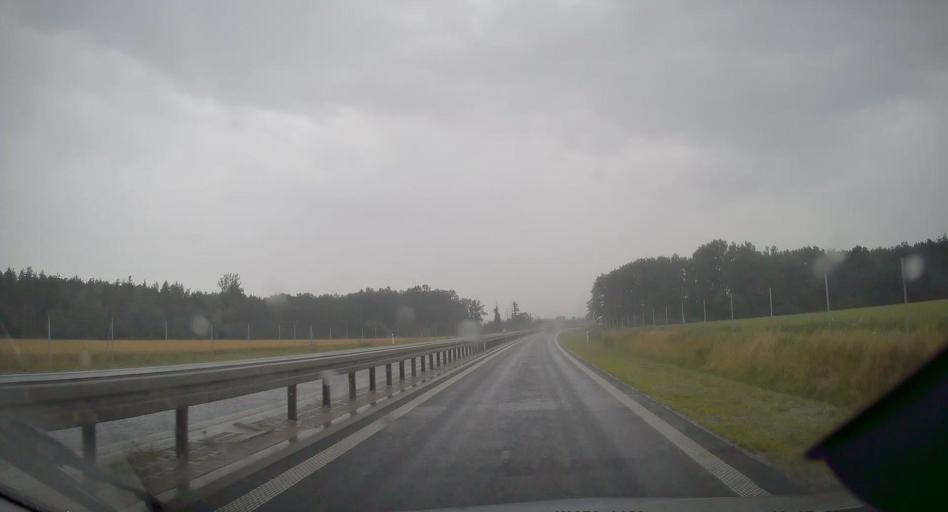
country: PL
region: Opole Voivodeship
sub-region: Powiat nyski
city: Nysa
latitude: 50.4565
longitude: 17.4035
